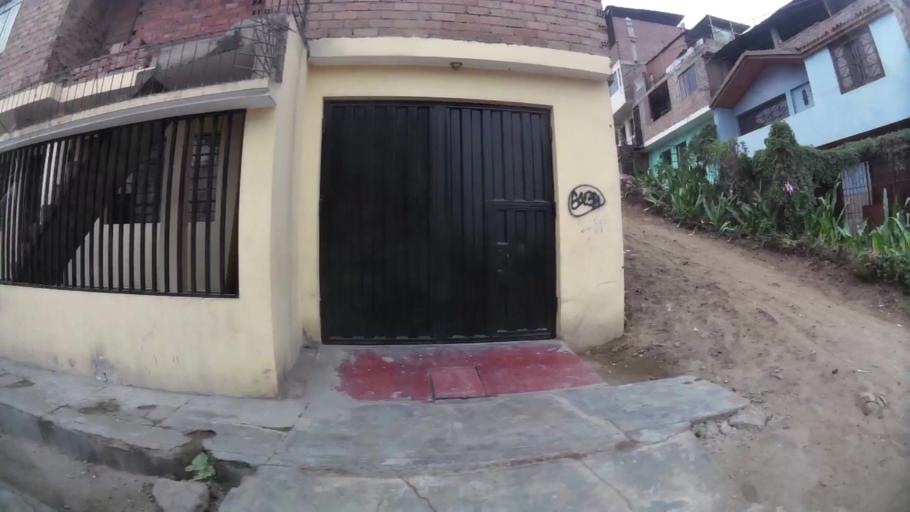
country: PE
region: Lima
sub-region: Lima
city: Surco
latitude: -12.1545
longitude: -76.9585
